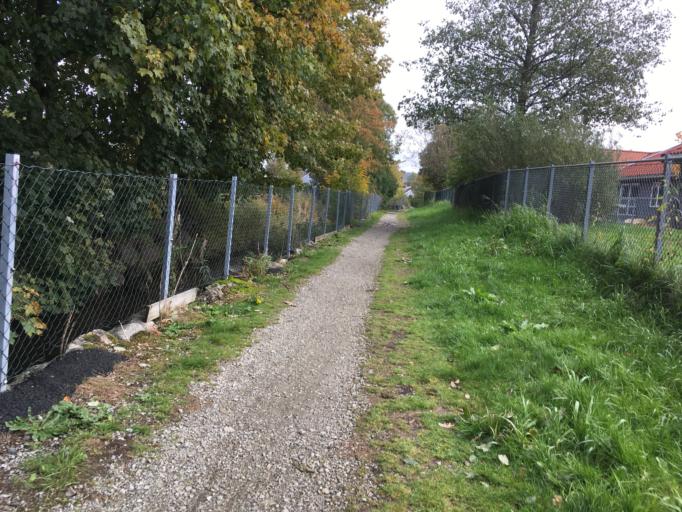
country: NO
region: Rogaland
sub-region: Sandnes
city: Sandnes
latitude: 58.8471
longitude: 5.7089
